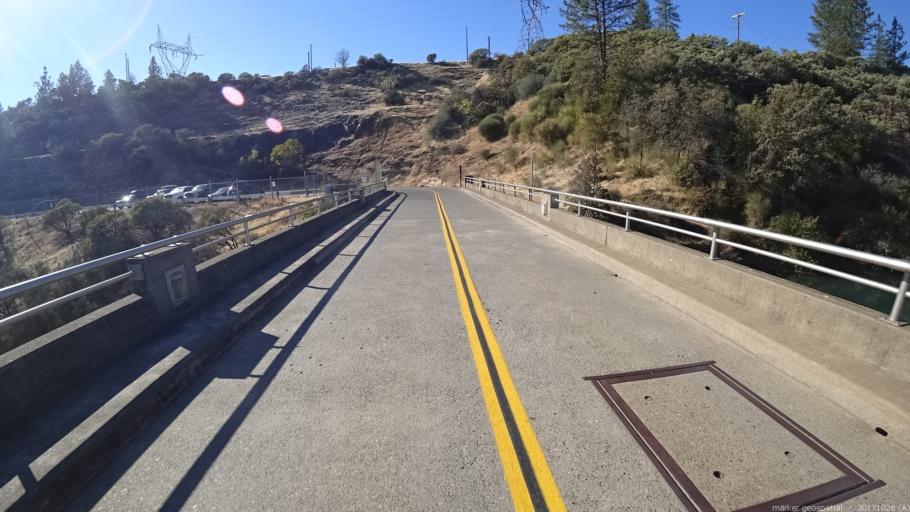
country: US
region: California
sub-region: Shasta County
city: Shasta
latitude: 40.6121
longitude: -122.4469
